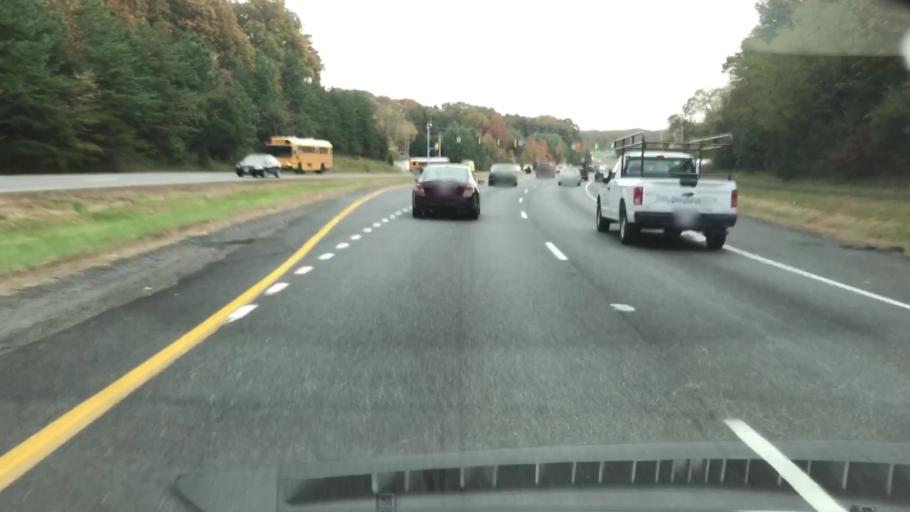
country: US
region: Virginia
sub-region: Fairfax County
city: Fairfax Station
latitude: 38.8215
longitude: -77.3502
